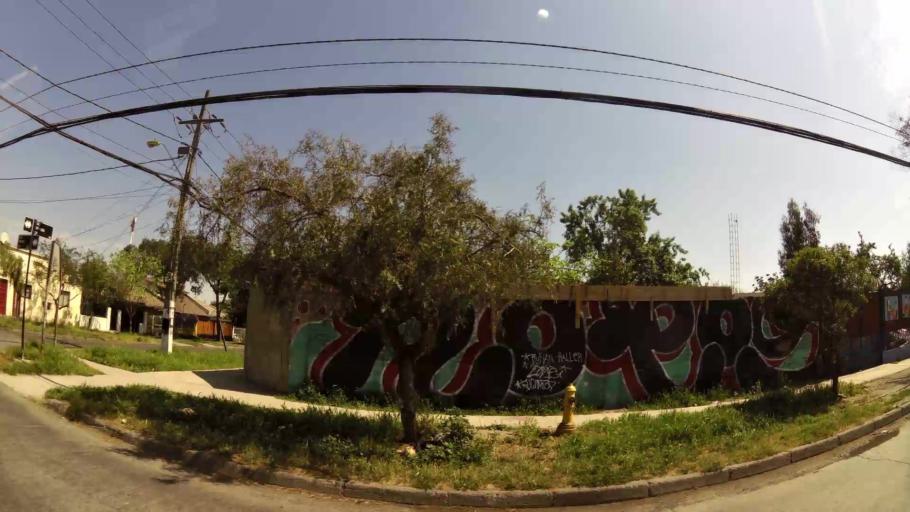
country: CL
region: Santiago Metropolitan
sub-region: Provincia de Santiago
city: La Pintana
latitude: -33.5479
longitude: -70.6643
